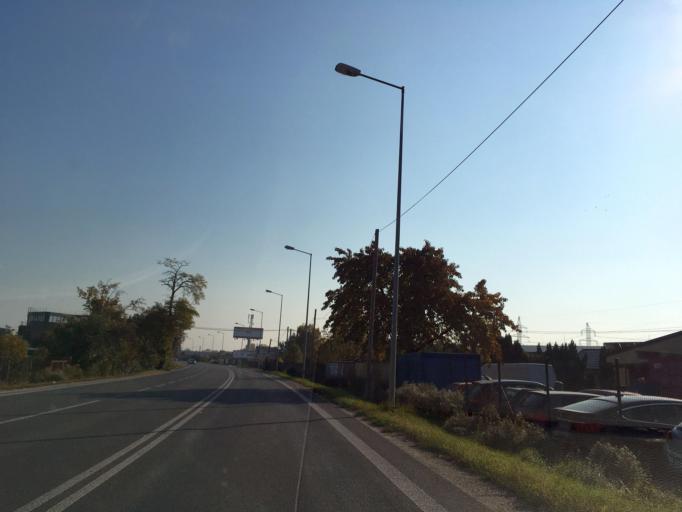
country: SK
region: Bratislavsky
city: Dunajska Luzna
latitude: 48.1249
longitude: 17.1979
